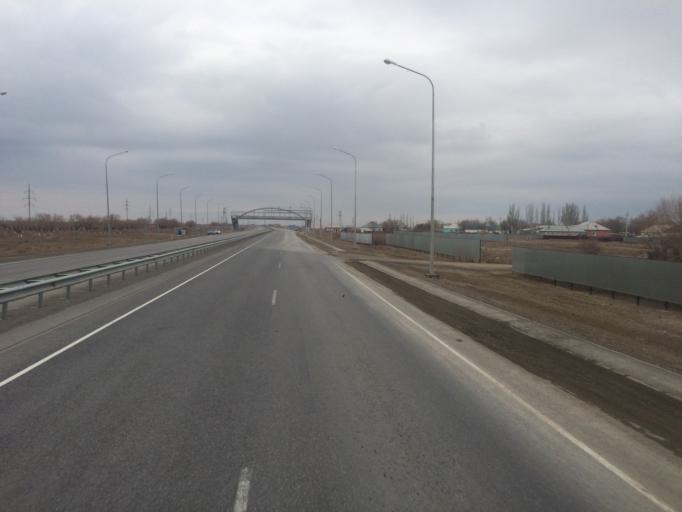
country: KZ
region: Qyzylorda
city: Shieli
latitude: 44.1362
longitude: 66.9710
